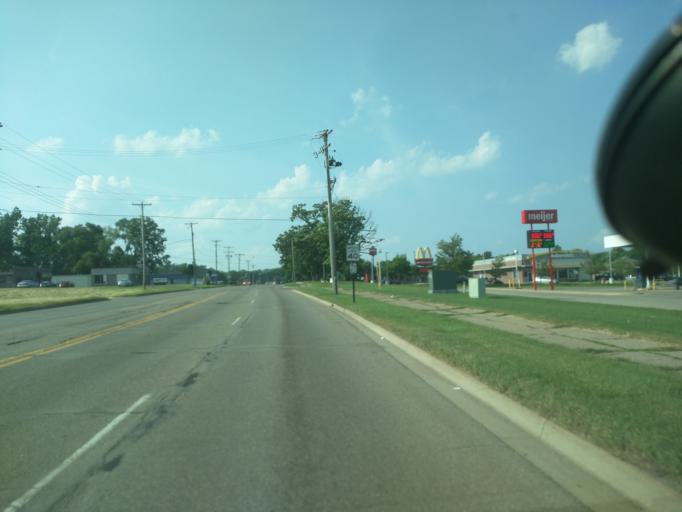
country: US
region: Michigan
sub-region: Jackson County
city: Jackson
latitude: 42.2713
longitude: -84.4529
